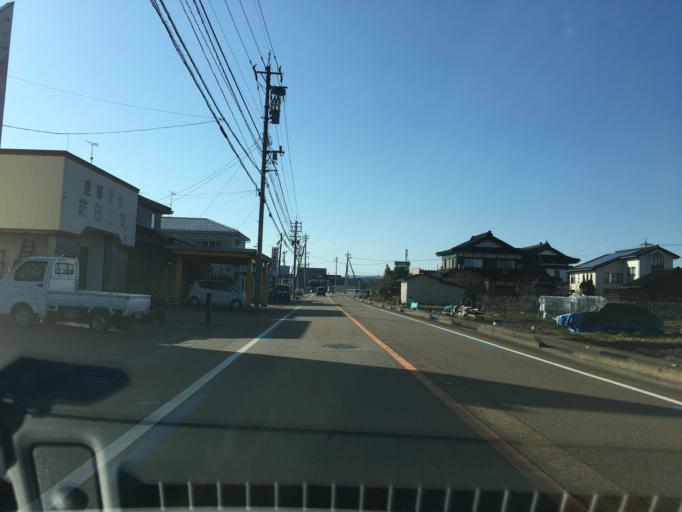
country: JP
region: Toyama
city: Himi
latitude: 36.8274
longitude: 137.0058
